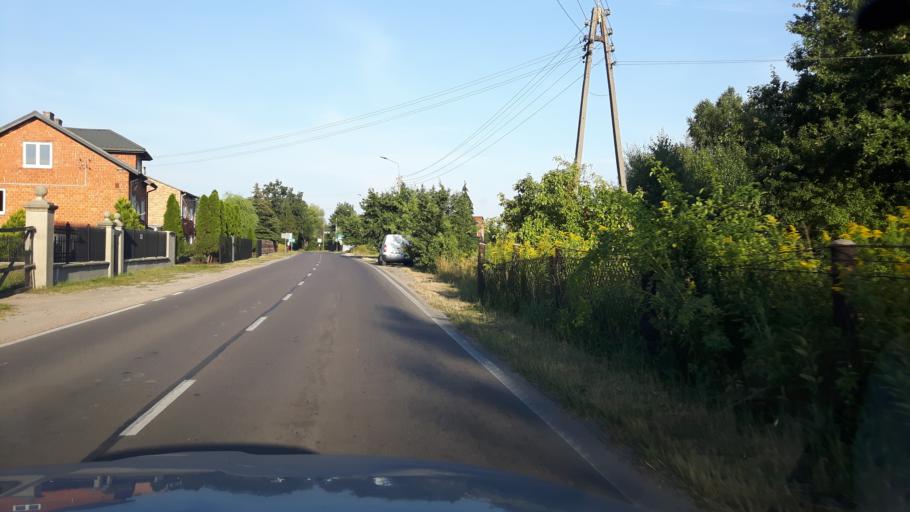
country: PL
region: Masovian Voivodeship
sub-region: Powiat wolominski
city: Kobylka
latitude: 52.3594
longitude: 21.1772
